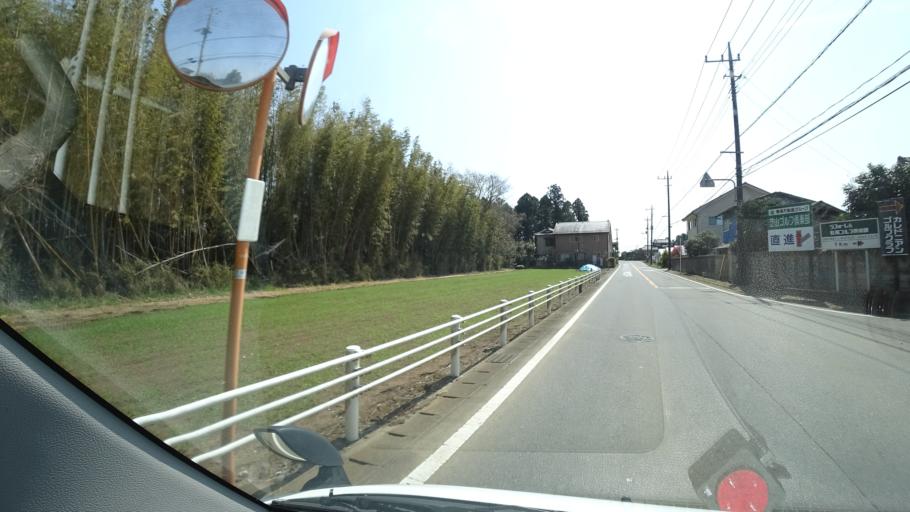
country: JP
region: Chiba
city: Yachimata
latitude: 35.7106
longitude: 140.4051
